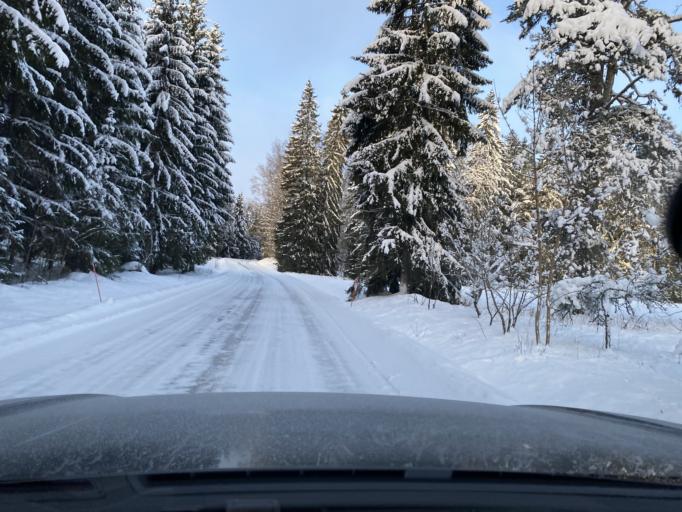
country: FI
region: Haeme
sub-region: Forssa
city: Tammela
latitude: 60.8628
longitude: 23.8927
